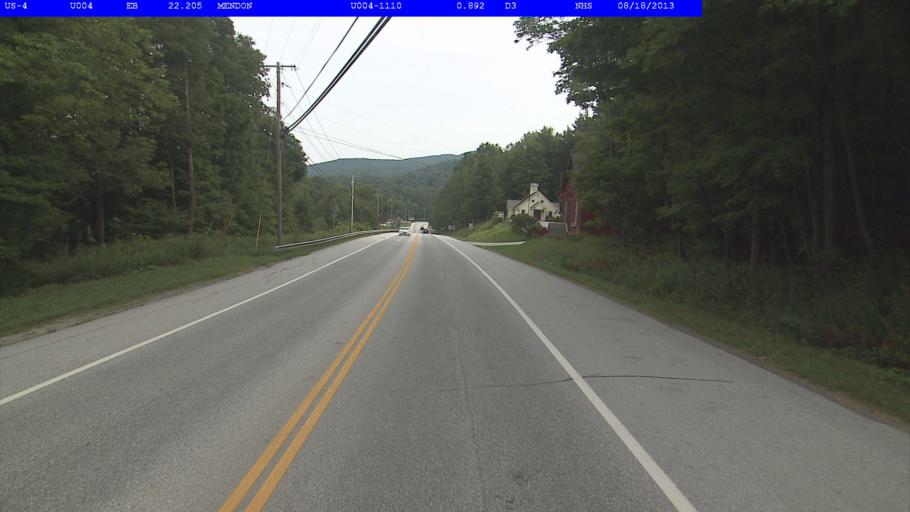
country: US
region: Vermont
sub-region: Rutland County
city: Rutland
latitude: 43.6462
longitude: -72.9291
